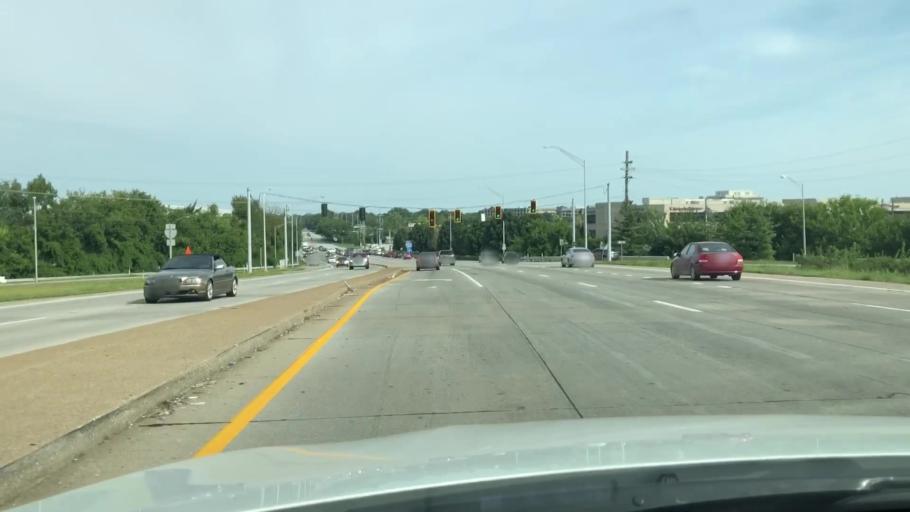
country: US
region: Kentucky
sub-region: Jefferson County
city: Saint Regis Park
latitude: 38.2292
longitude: -85.6365
